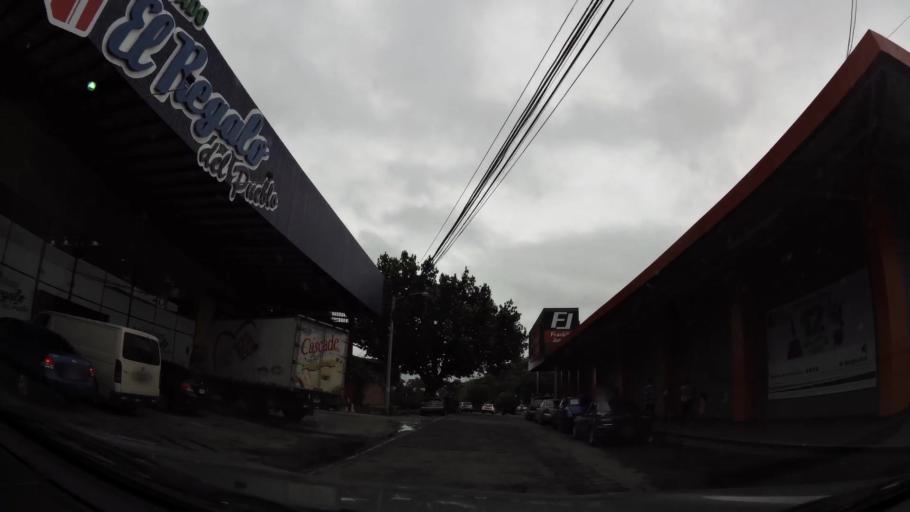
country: PA
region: Chiriqui
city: La Concepcion
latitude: 8.5168
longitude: -82.6203
